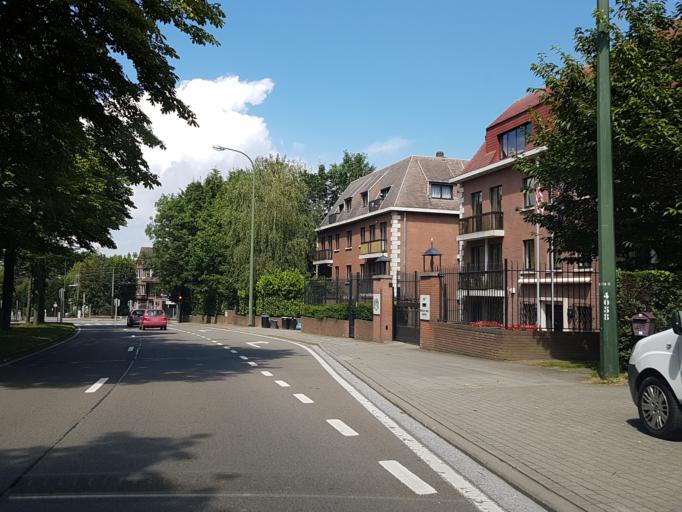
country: BE
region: Flanders
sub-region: Provincie Vlaams-Brabant
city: Kraainem
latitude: 50.8261
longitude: 4.4461
